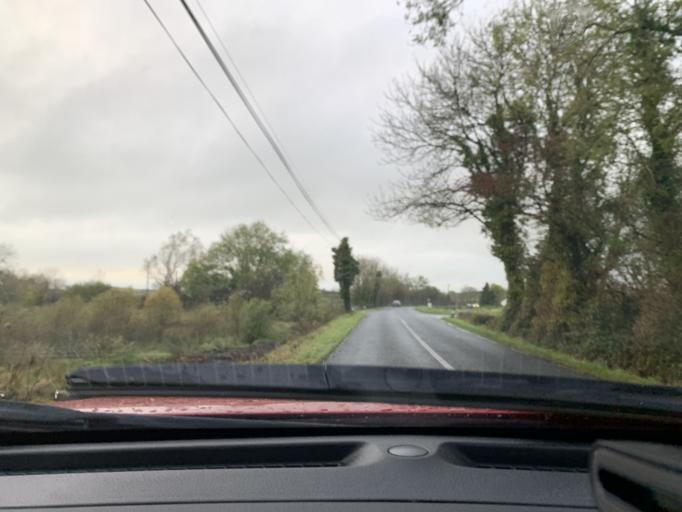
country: IE
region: Connaught
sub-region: Sligo
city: Ballymote
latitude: 54.0177
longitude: -8.5233
